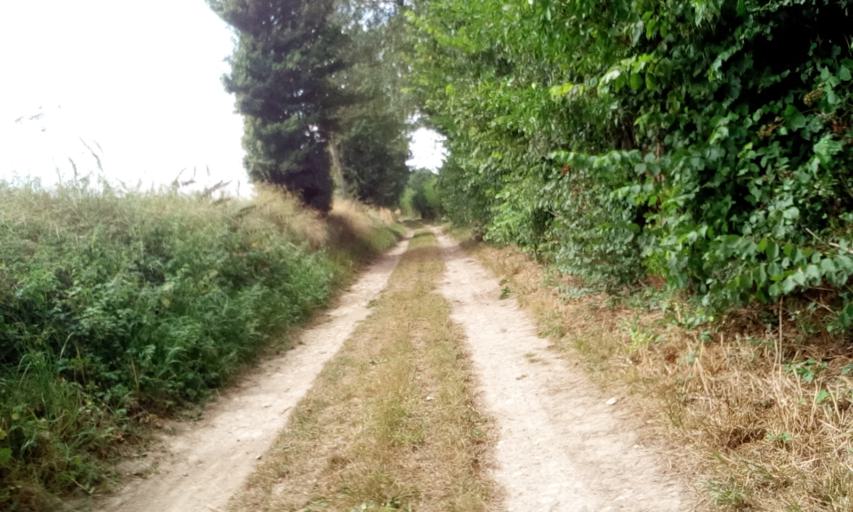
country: FR
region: Lower Normandy
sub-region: Departement du Calvados
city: Creully
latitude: 49.2901
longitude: -0.4998
